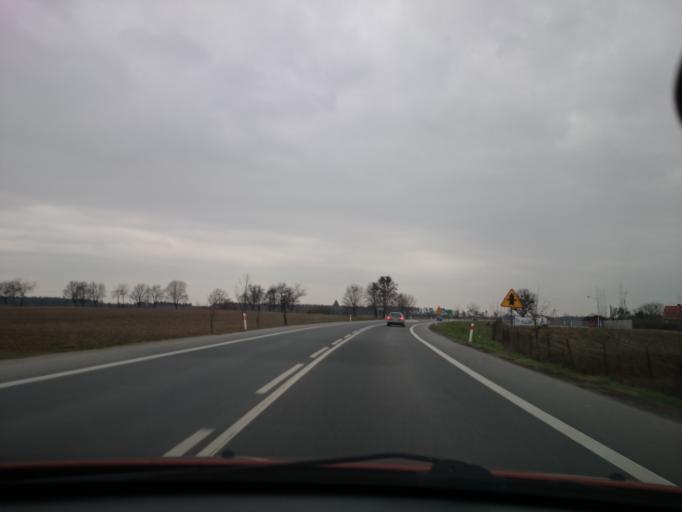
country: PL
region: Opole Voivodeship
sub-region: Powiat nyski
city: Lambinowice
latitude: 50.5956
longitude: 17.5314
